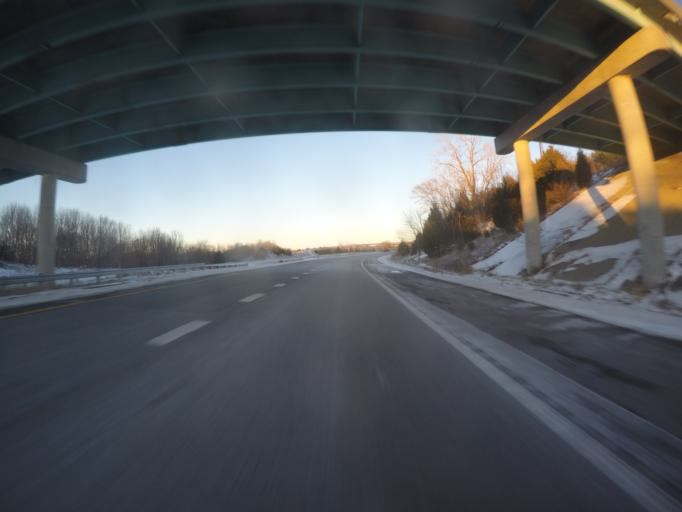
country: US
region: Missouri
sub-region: Platte County
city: Platte City
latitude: 39.3391
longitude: -94.7520
